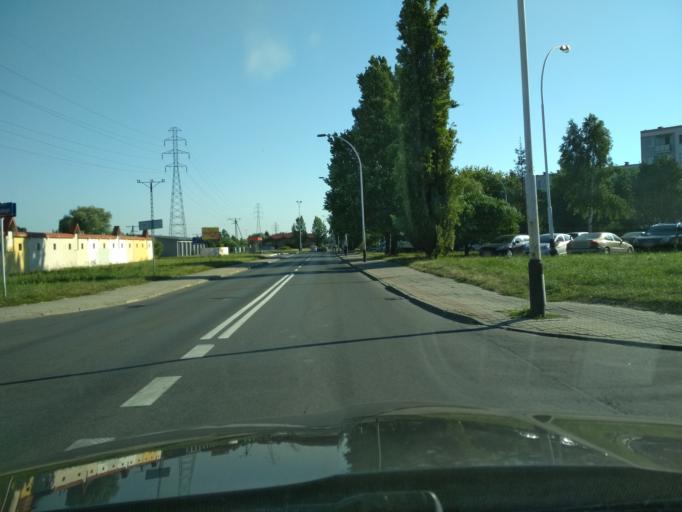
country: PL
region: Subcarpathian Voivodeship
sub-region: Rzeszow
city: Rzeszow
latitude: 50.0613
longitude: 21.9788
